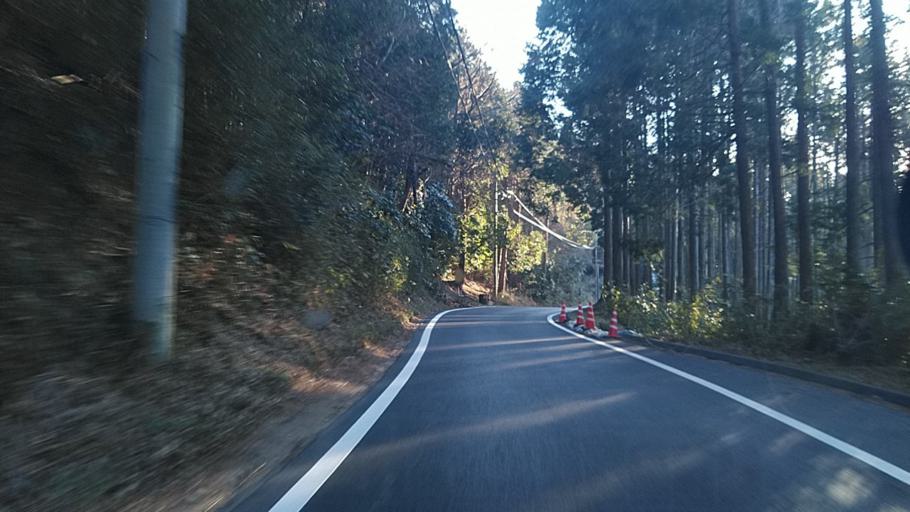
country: JP
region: Chiba
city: Kimitsu
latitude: 35.2542
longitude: 139.9530
